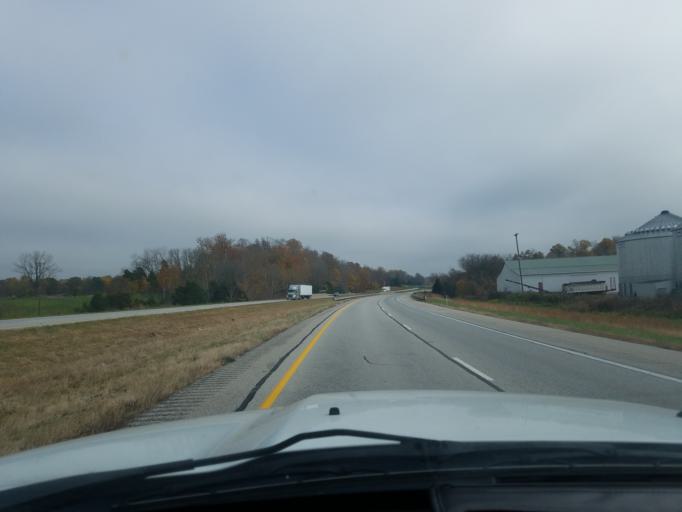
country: US
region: Indiana
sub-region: Harrison County
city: Corydon
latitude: 38.2464
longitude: -86.0861
